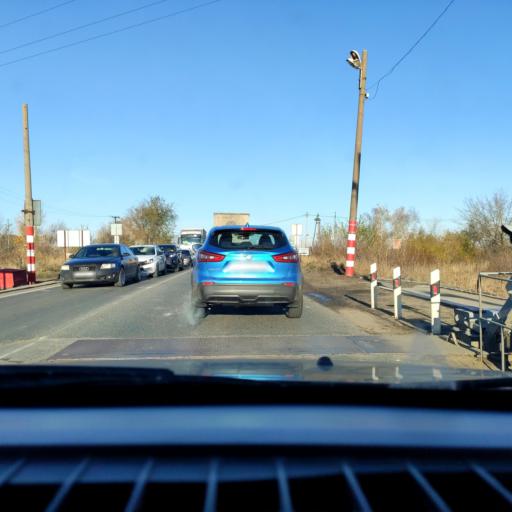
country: RU
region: Samara
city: Tol'yatti
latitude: 53.5617
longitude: 49.3564
